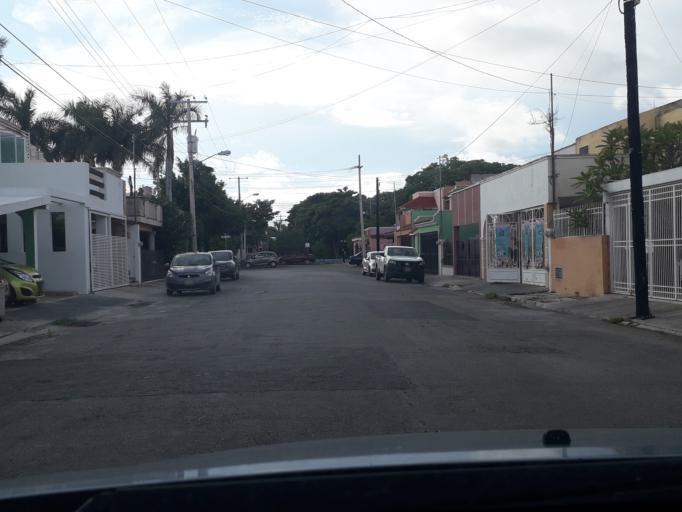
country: MX
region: Yucatan
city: Merida
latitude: 21.0078
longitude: -89.6385
